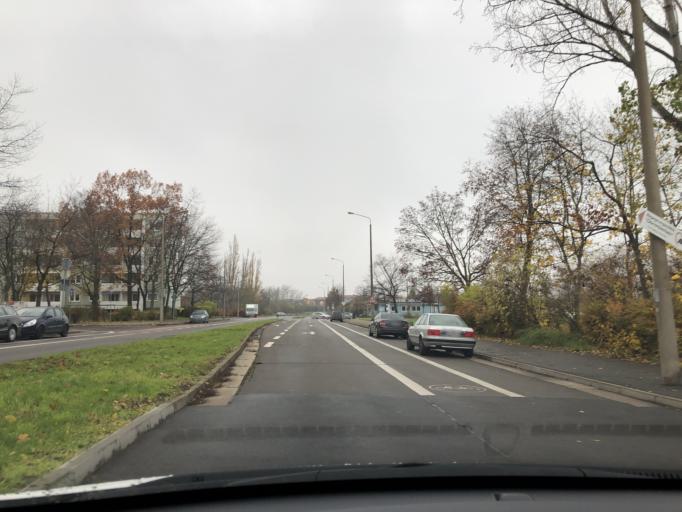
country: DE
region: Saxony-Anhalt
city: Halle Neustadt
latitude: 51.4847
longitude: 11.9282
